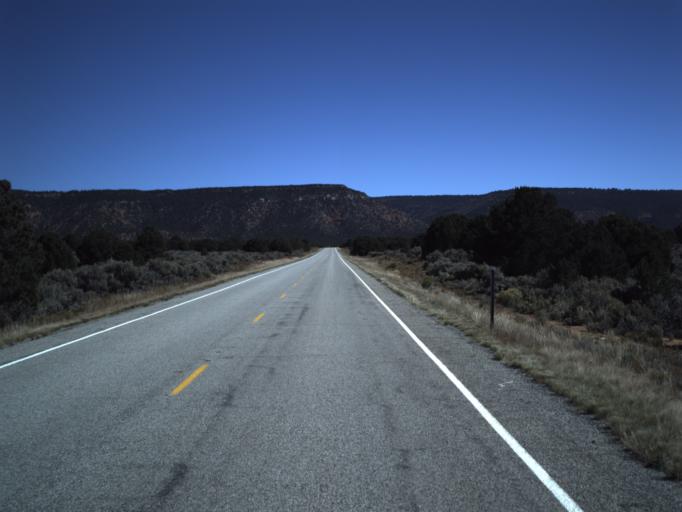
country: US
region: Utah
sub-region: San Juan County
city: Blanding
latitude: 37.5829
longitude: -109.9104
